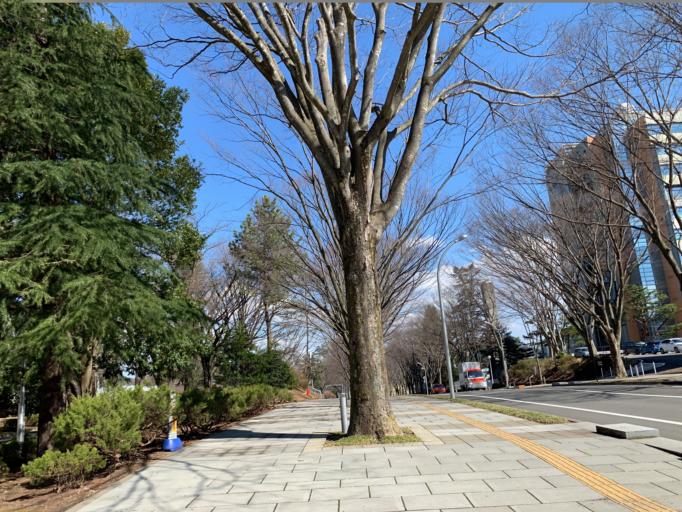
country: JP
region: Miyagi
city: Sendai
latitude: 38.2556
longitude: 140.8386
